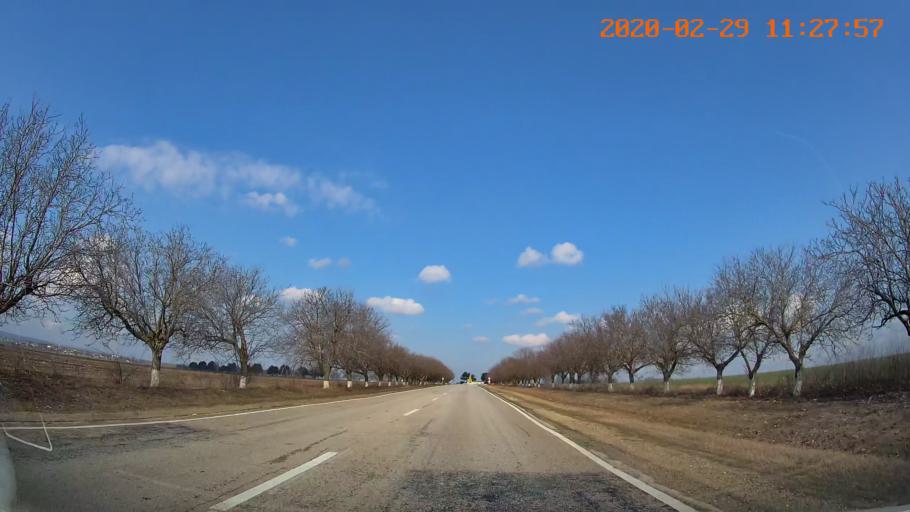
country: MD
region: Telenesti
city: Cocieri
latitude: 47.4762
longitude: 29.1403
